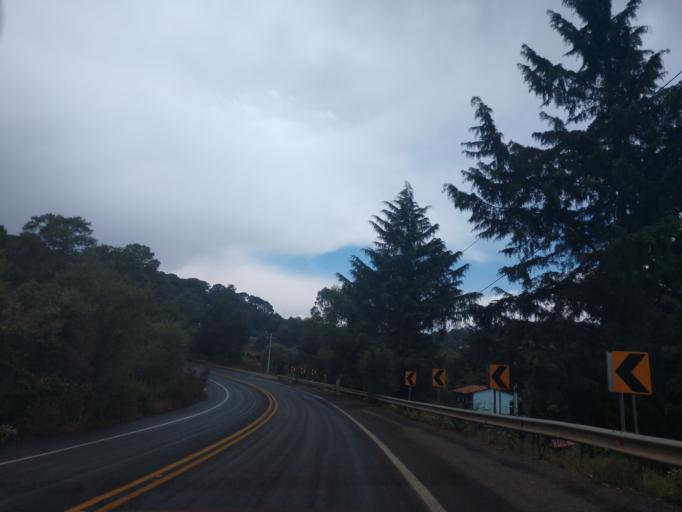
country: MX
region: Jalisco
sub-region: Mazamitla
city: Mazamitla
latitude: 19.9417
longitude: -103.0613
